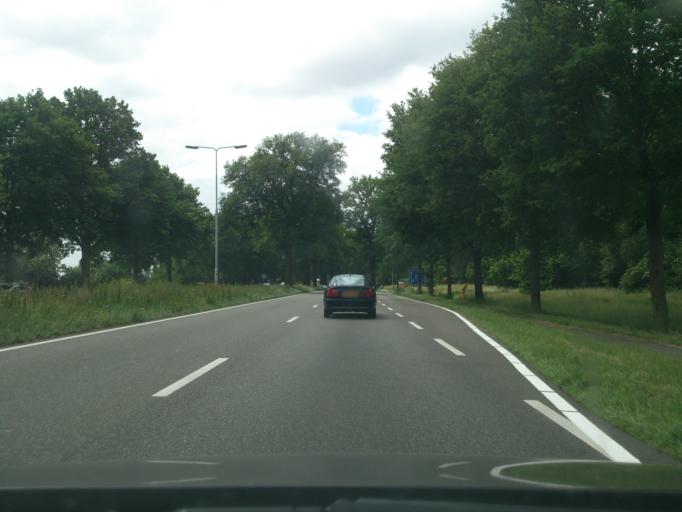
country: NL
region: North Brabant
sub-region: Gemeente Oisterwijk
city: Oisterwijk
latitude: 51.5854
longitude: 5.1586
